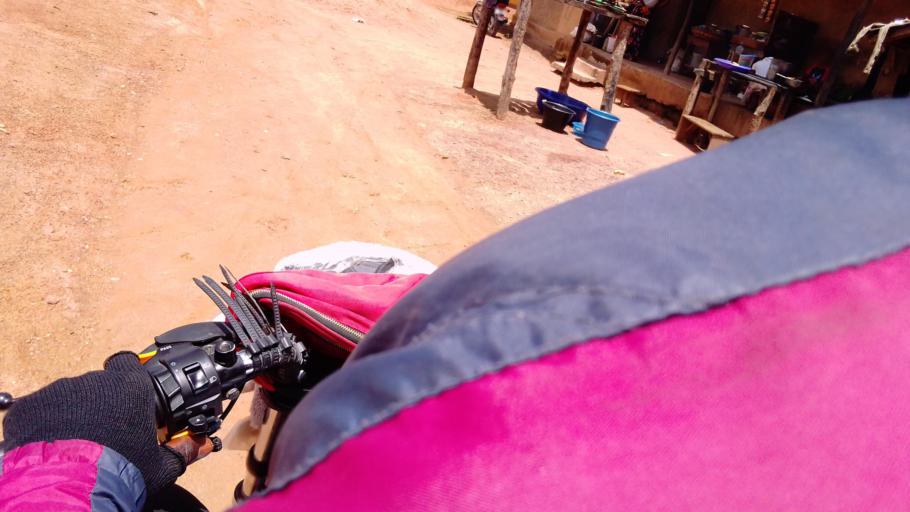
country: SL
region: Eastern Province
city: Koidu
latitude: 8.6988
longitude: -10.9532
